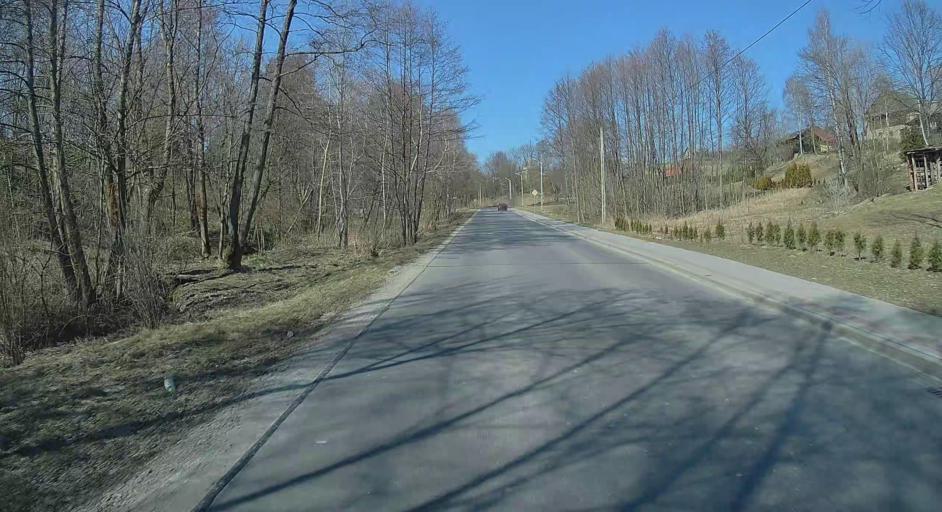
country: PL
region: Subcarpathian Voivodeship
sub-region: Powiat rzeszowski
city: Hyzne
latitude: 49.8894
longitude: 22.2273
